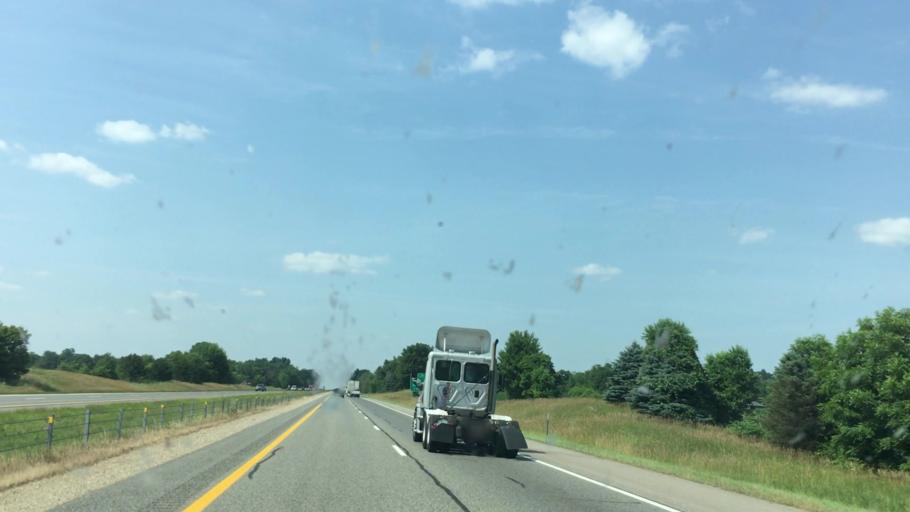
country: US
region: Michigan
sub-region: Allegan County
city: Otsego
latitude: 42.5172
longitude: -85.6561
